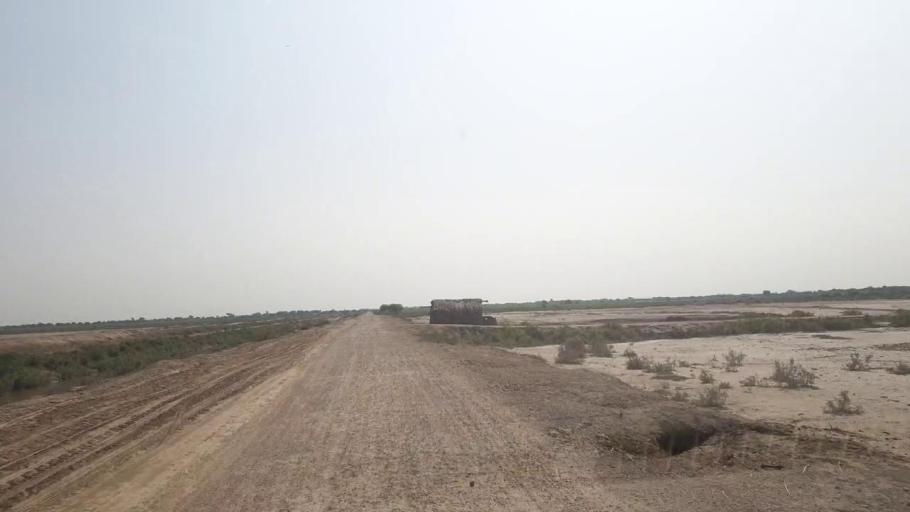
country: PK
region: Sindh
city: Kadhan
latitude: 24.4744
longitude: 68.9029
